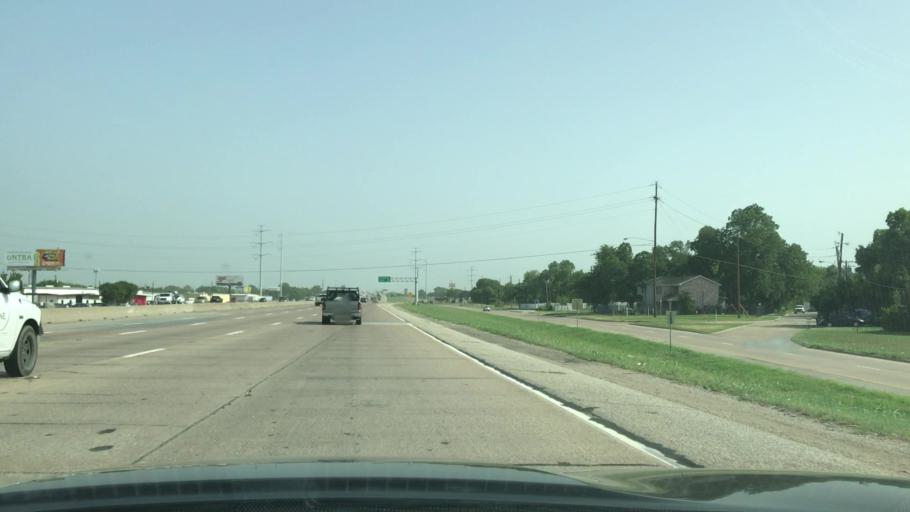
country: US
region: Texas
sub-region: Dallas County
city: Cockrell Hill
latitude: 32.7716
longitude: -96.9153
